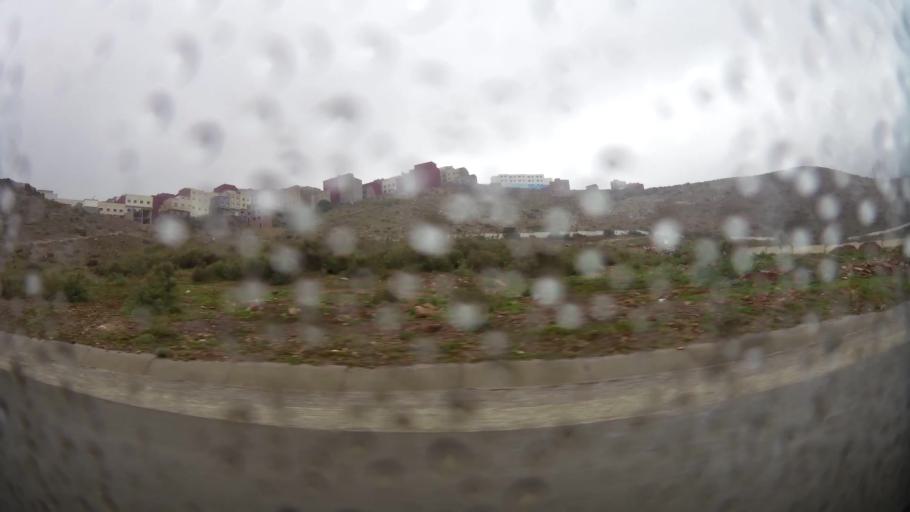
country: MA
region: Taza-Al Hoceima-Taounate
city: Al Hoceima
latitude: 35.2568
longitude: -3.9410
